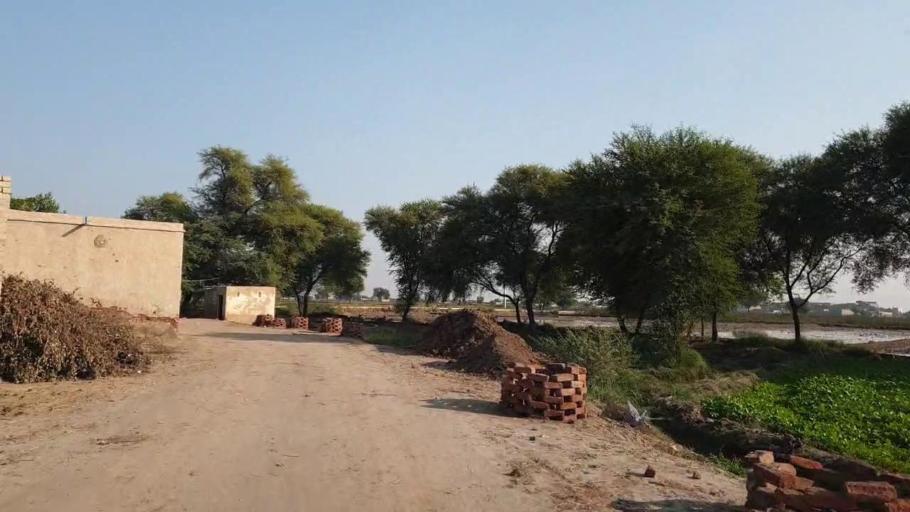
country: PK
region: Sindh
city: Sehwan
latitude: 26.4347
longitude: 67.7930
